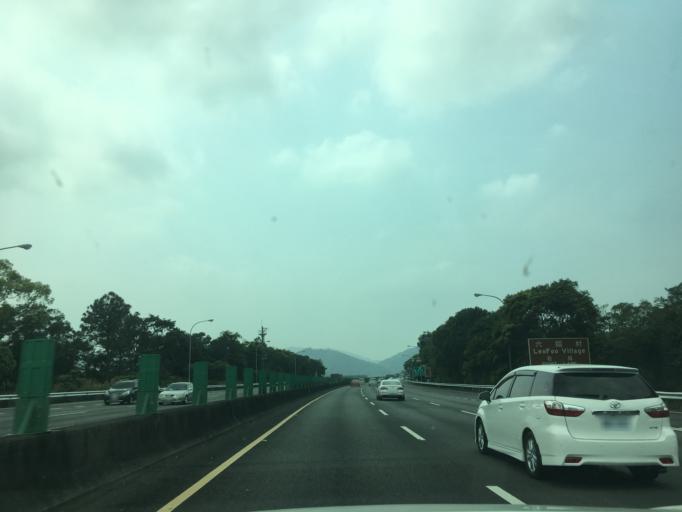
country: TW
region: Taiwan
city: Daxi
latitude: 24.7986
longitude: 121.1913
